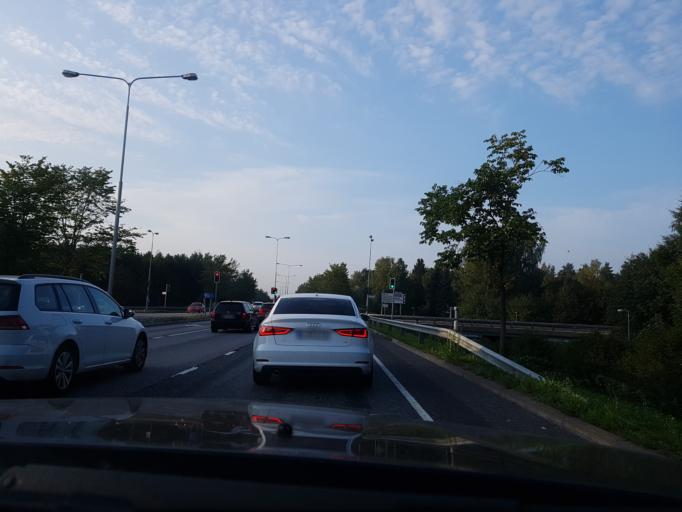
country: FI
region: Uusimaa
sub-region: Helsinki
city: Tuusula
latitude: 60.3883
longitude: 25.0250
